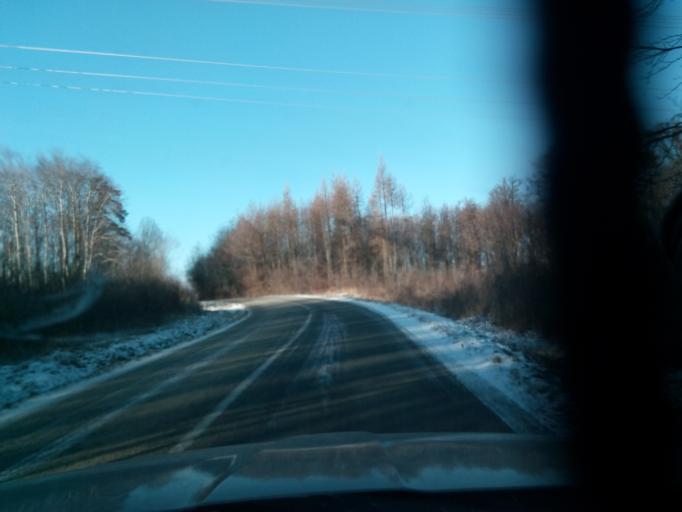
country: SK
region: Kosicky
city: Kosice
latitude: 48.7084
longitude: 21.1712
